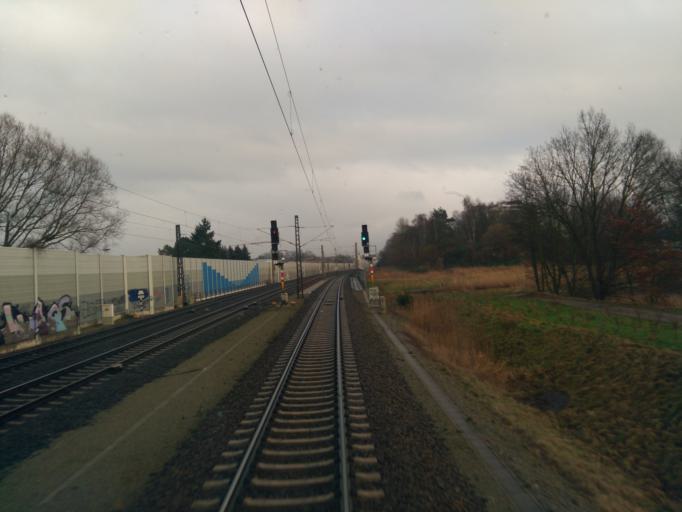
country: DE
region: Lower Saxony
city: Winsen
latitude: 53.3565
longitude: 10.1981
